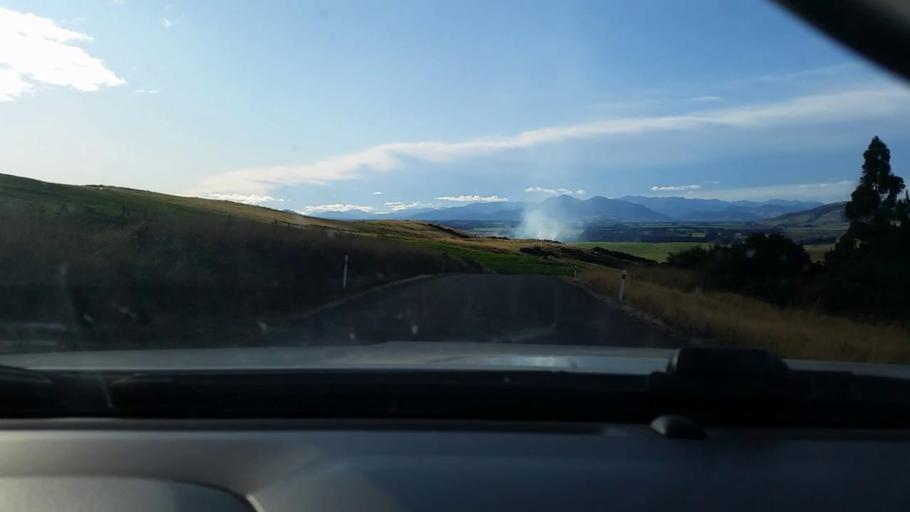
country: NZ
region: Southland
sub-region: Southland District
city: Winton
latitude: -45.8206
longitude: 168.1738
